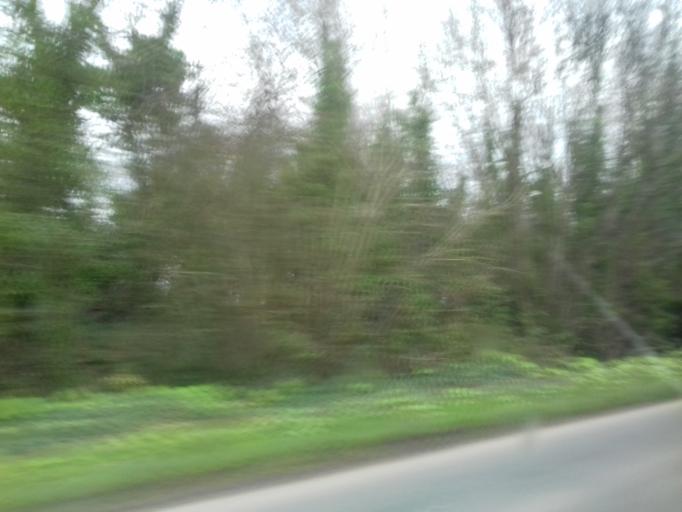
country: IE
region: Leinster
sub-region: An Mhi
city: Duleek
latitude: 53.6953
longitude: -6.4095
